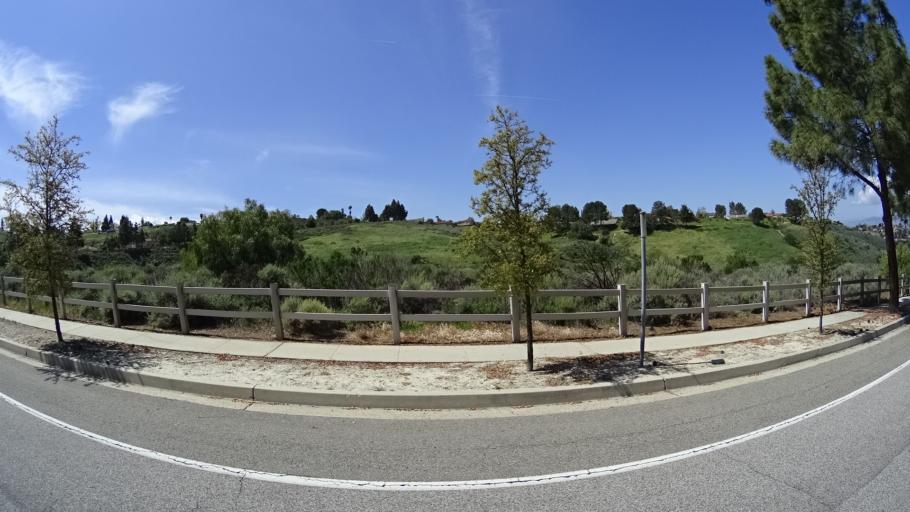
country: US
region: California
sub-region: Ventura County
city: Thousand Oaks
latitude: 34.2314
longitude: -118.8379
